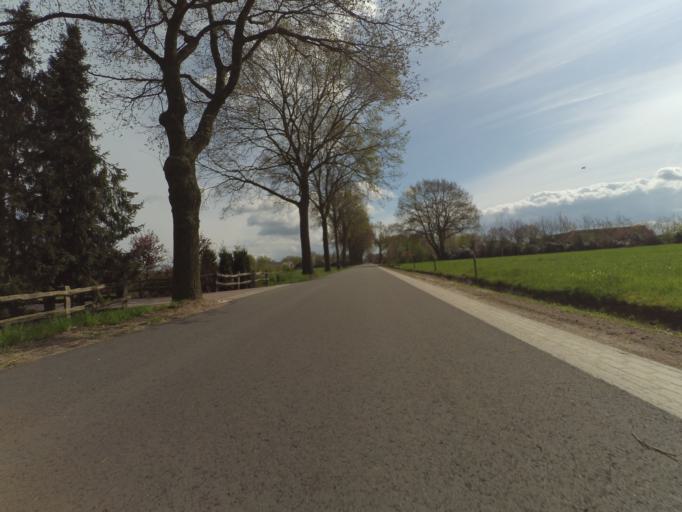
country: NL
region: Gelderland
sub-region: Gemeente Putten
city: Putten
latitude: 52.2397
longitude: 5.5778
